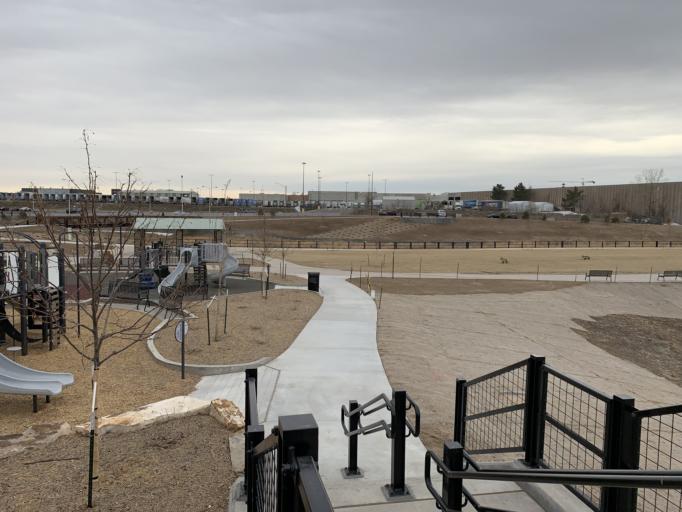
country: US
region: Colorado
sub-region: Denver County
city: Denver
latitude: 39.7778
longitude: -104.9770
